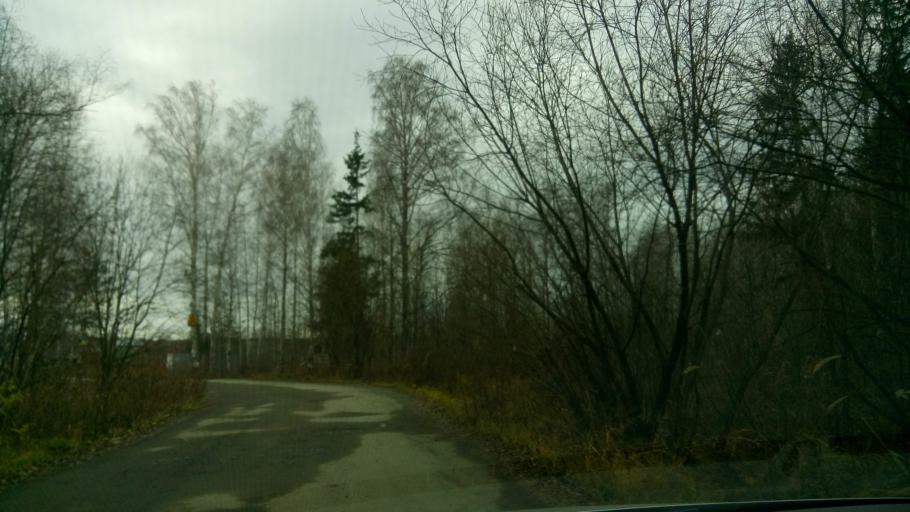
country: RU
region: Sverdlovsk
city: Sredneuralsk
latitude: 56.9700
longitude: 60.4722
